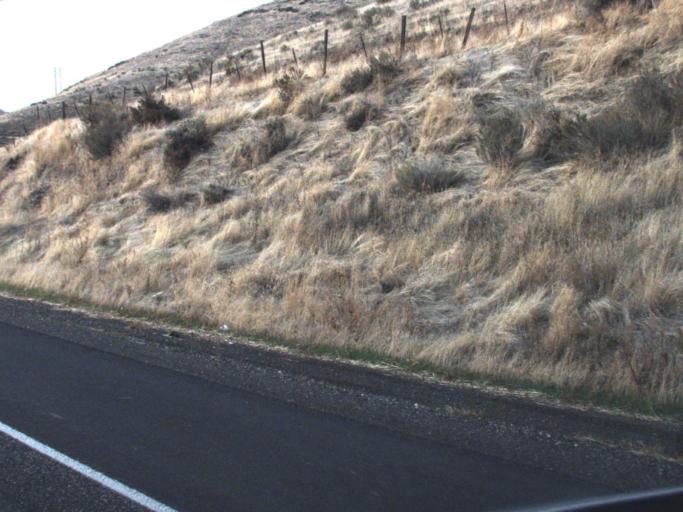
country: US
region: Washington
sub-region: Asotin County
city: Clarkston Heights-Vineland
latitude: 46.4031
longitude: -117.2405
